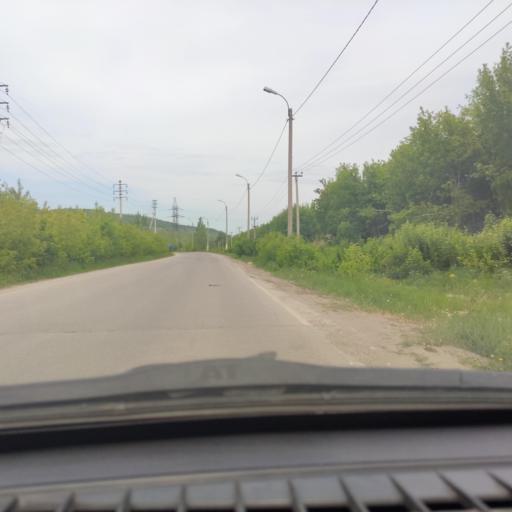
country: RU
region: Samara
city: Zhigulevsk
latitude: 53.4102
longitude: 49.4850
